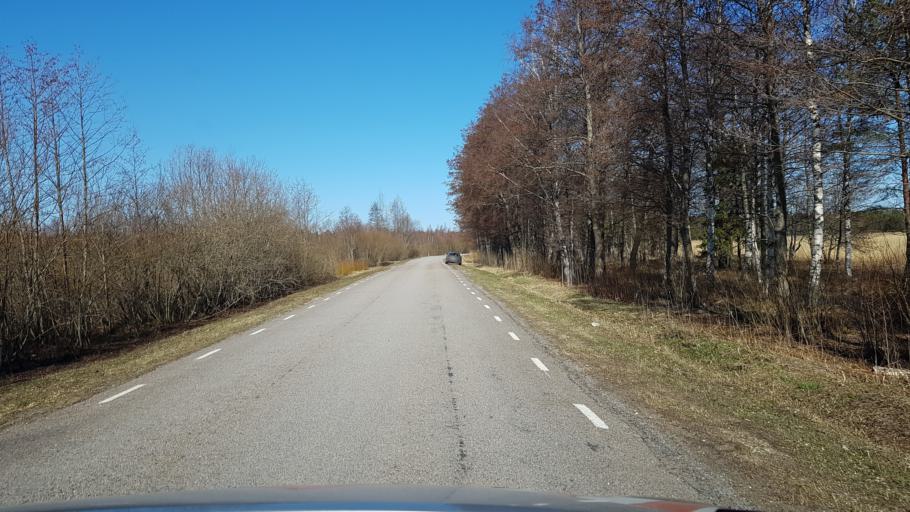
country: EE
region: Harju
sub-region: Loksa linn
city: Loksa
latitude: 59.5813
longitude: 25.9146
